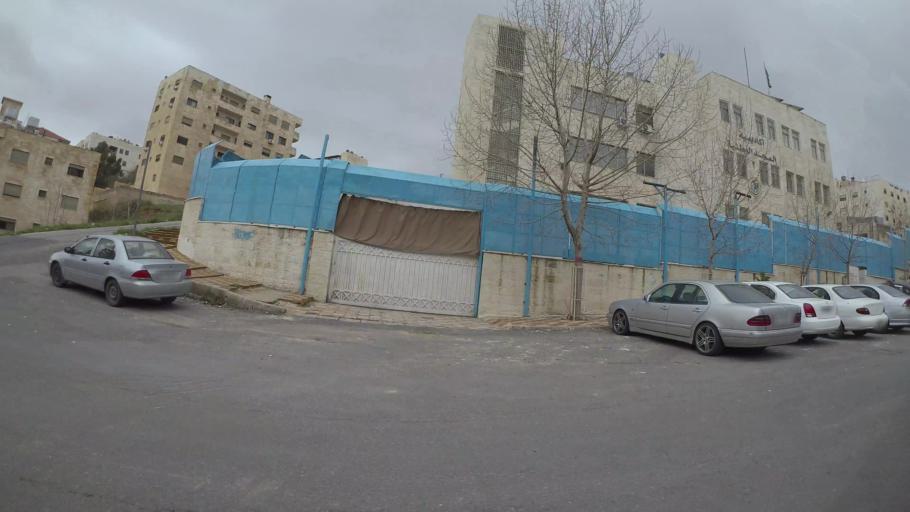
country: JO
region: Amman
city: Wadi as Sir
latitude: 31.9664
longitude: 35.8316
